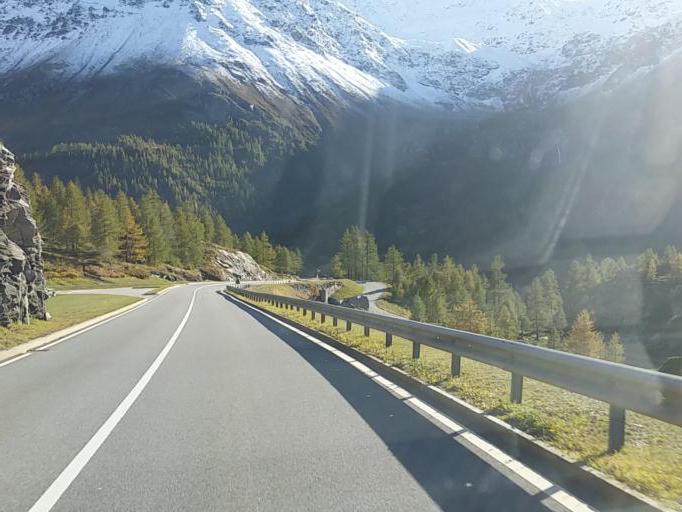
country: CH
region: Valais
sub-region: Brig District
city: Brig
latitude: 46.2320
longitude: 8.0143
